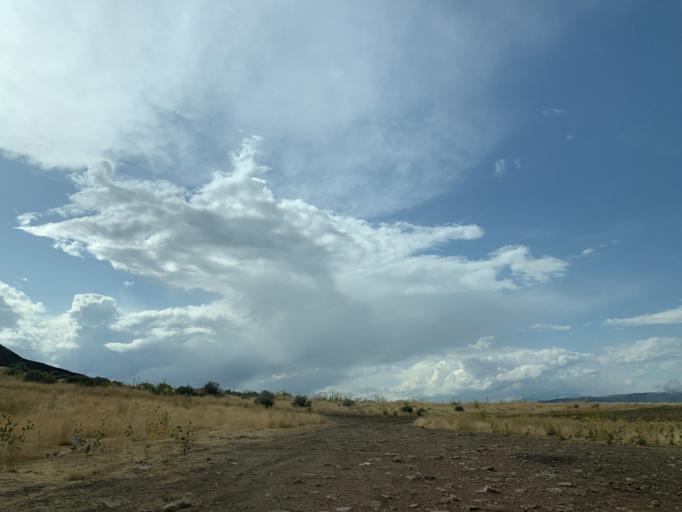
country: US
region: Utah
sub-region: Utah County
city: West Mountain
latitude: 40.1220
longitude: -111.8156
